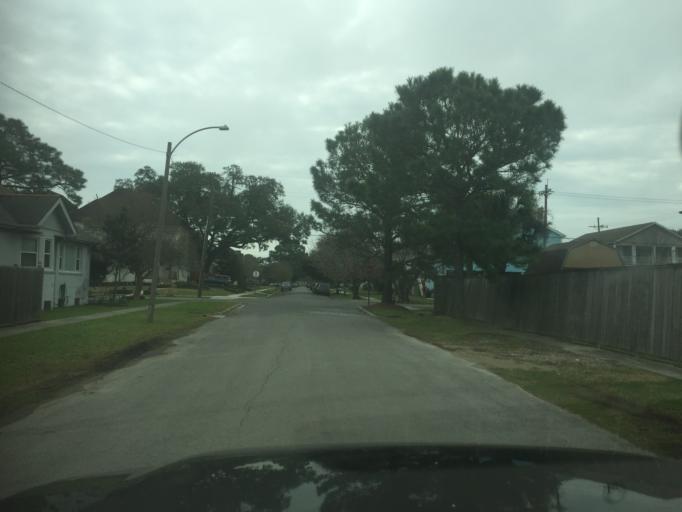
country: US
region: Louisiana
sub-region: Jefferson Parish
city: Metairie
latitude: 29.9994
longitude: -90.1054
